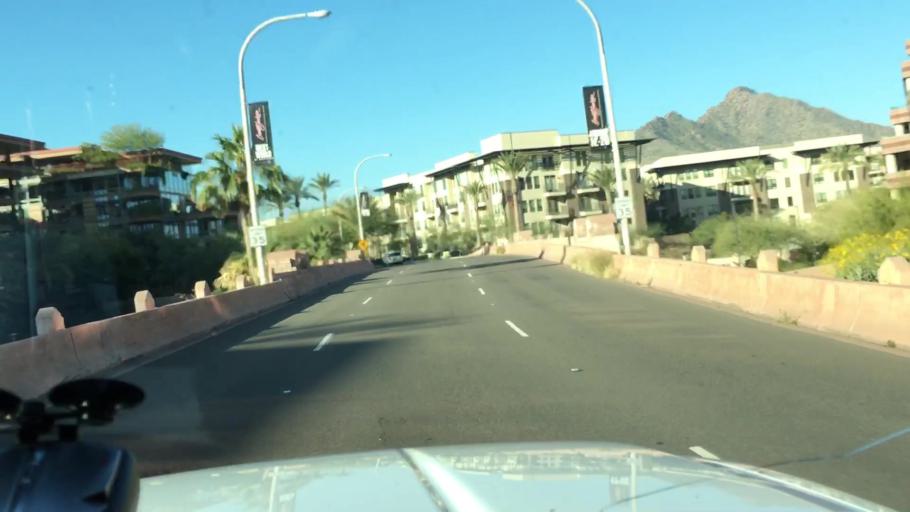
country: US
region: Arizona
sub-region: Maricopa County
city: Paradise Valley
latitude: 33.5076
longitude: -111.9277
